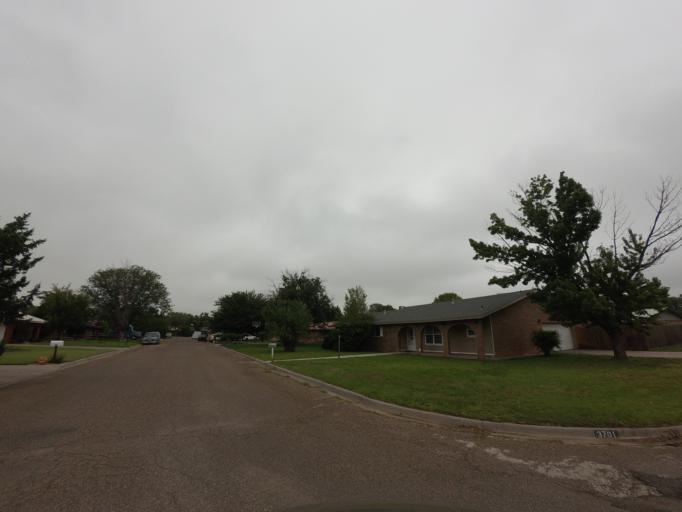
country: US
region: New Mexico
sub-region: Curry County
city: Clovis
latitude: 34.4365
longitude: -103.1932
